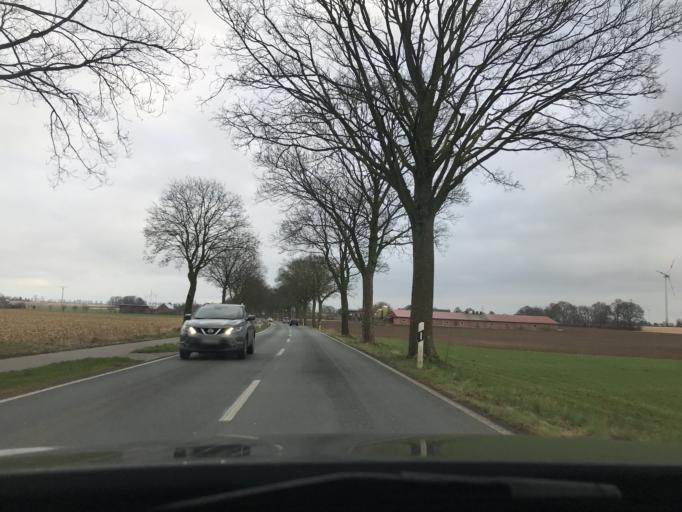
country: DE
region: North Rhine-Westphalia
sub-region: Regierungsbezirk Dusseldorf
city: Goch
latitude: 51.7346
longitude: 6.2022
